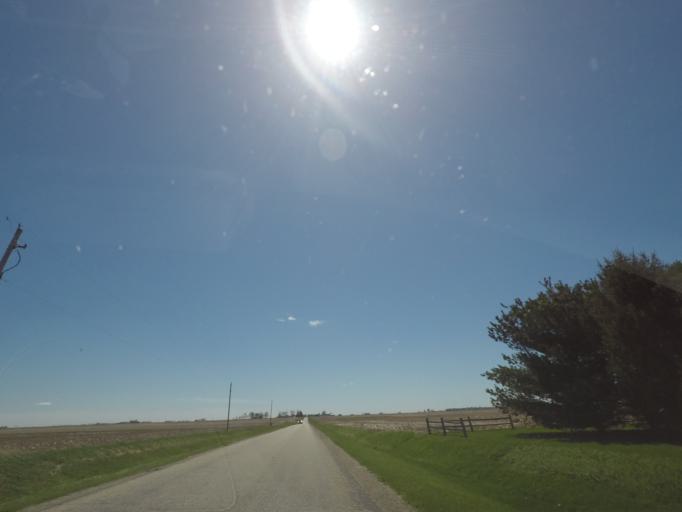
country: US
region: Illinois
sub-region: Logan County
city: Atlanta
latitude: 40.1803
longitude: -89.1939
